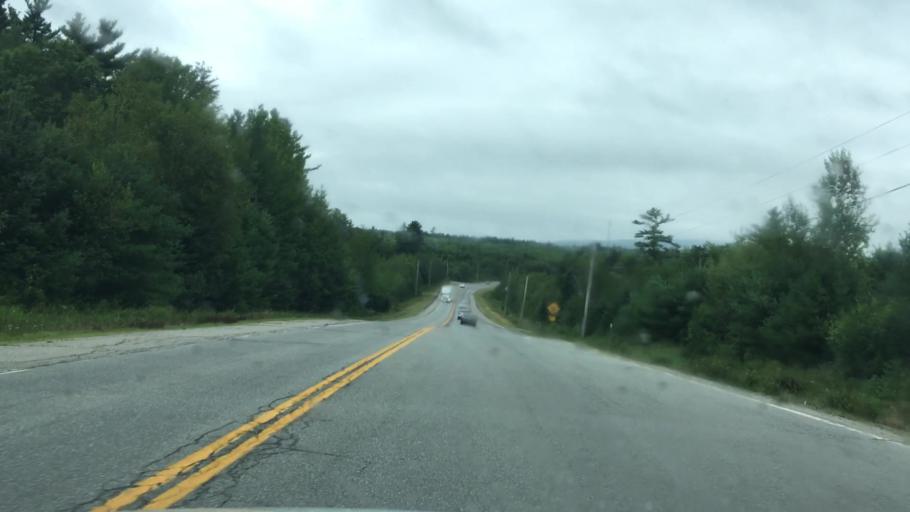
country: US
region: Maine
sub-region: Washington County
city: Cherryfield
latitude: 44.8494
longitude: -68.0610
